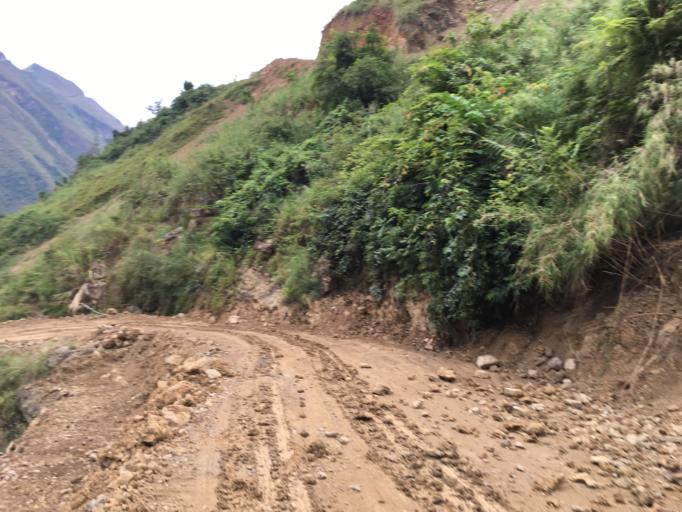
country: CN
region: Guizhou Sheng
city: Anshun
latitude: 25.9624
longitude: 105.2436
